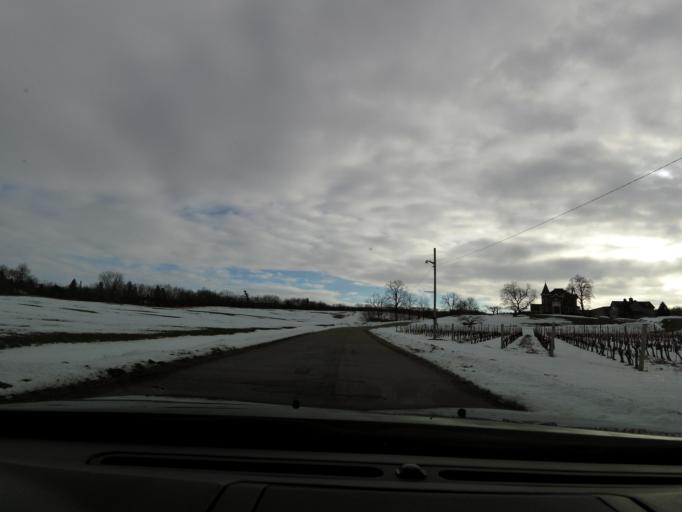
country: CA
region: Ontario
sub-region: Regional Municipality of Niagara
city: St. Catharines
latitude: 43.1782
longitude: -79.5077
